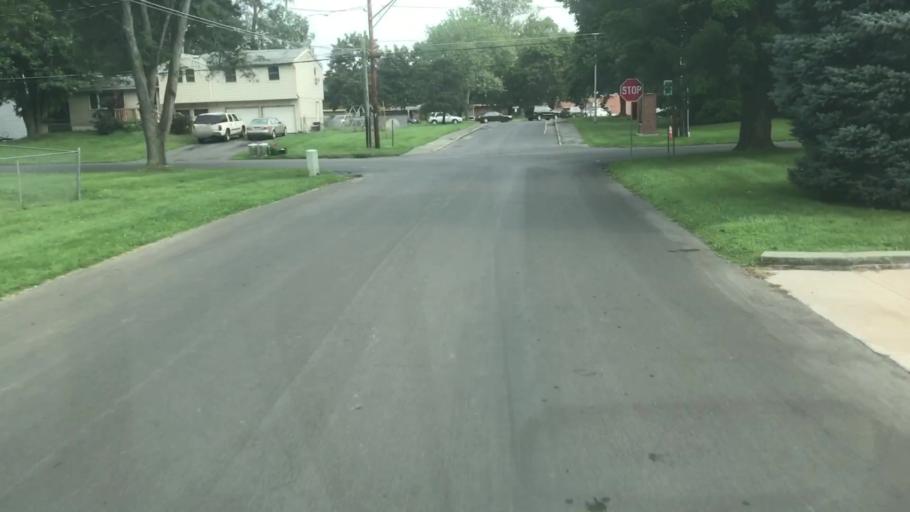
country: US
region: New York
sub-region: Onondaga County
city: Liverpool
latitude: 43.1400
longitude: -76.2243
